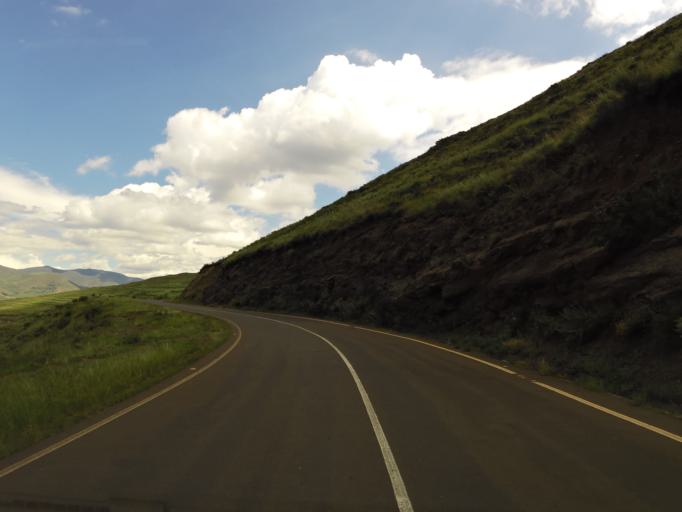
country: LS
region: Thaba-Tseka
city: Thaba-Tseka
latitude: -29.1519
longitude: 28.4796
